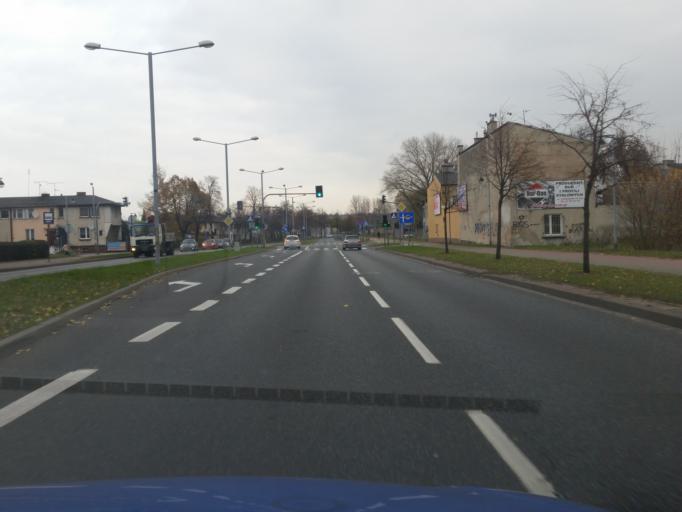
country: PL
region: Silesian Voivodeship
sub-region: Czestochowa
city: Czestochowa
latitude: 50.8052
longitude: 19.1389
